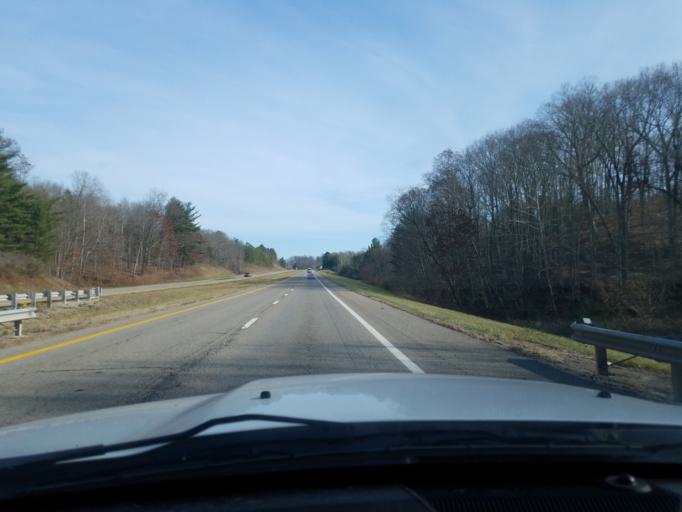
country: US
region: Ohio
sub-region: Vinton County
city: McArthur
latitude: 39.1678
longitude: -82.3129
